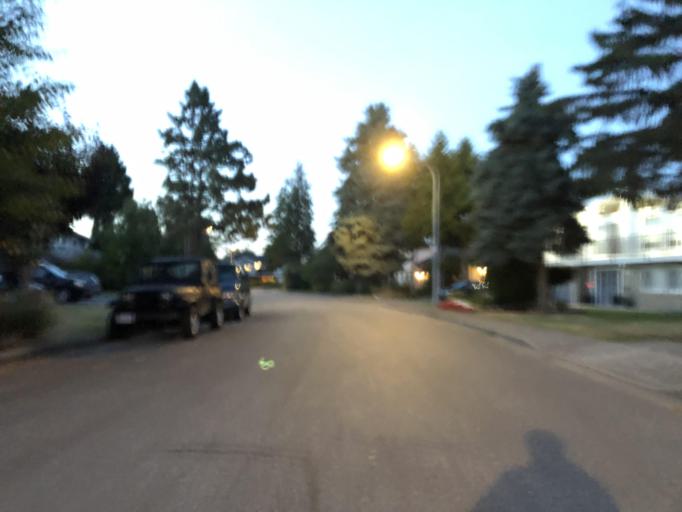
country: CA
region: British Columbia
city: Richmond
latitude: 49.1465
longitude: -123.1117
